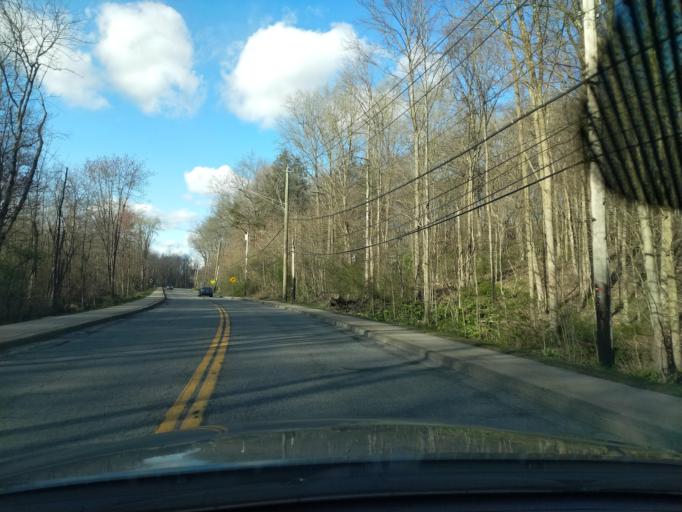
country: US
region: New York
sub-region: Westchester County
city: Mount Kisco
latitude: 41.2089
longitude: -73.7239
